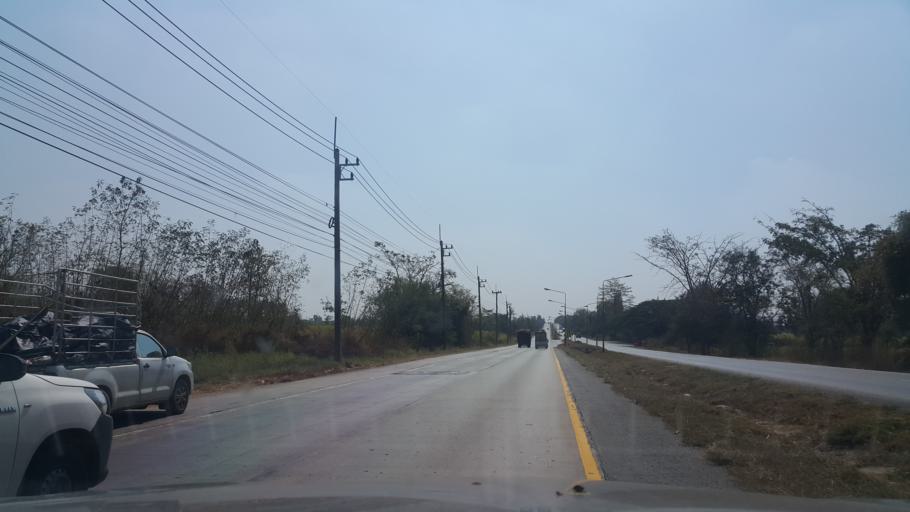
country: TH
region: Khon Kaen
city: Nam Phong
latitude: 16.8098
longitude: 102.8345
